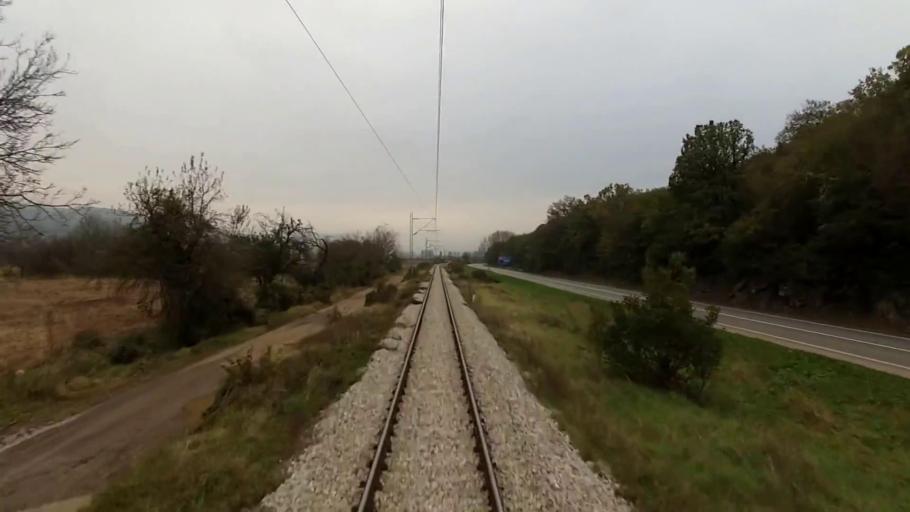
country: RS
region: Central Serbia
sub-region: Pirotski Okrug
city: Dimitrovgrad
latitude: 43.0120
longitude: 22.7987
